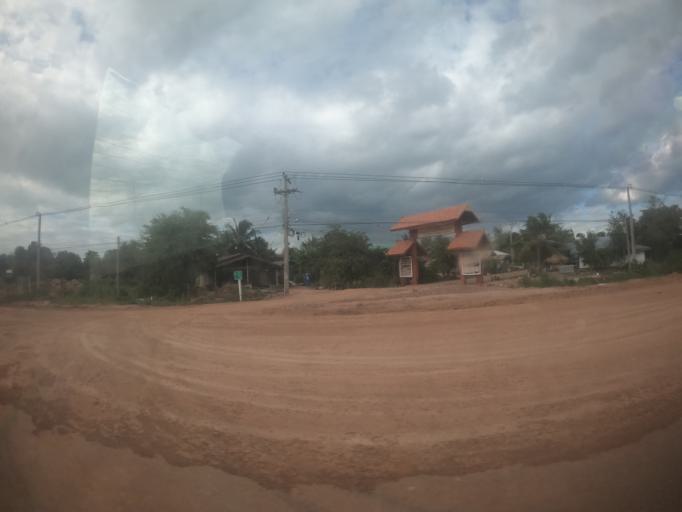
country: TH
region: Surin
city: Kap Choeng
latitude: 14.5083
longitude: 103.5551
